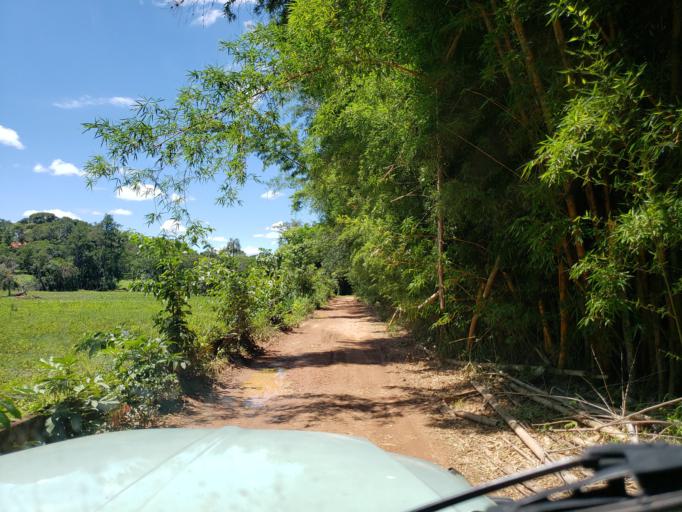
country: BR
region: Sao Paulo
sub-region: Moji-Guacu
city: Mogi-Gaucu
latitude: -22.3117
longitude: -46.8785
